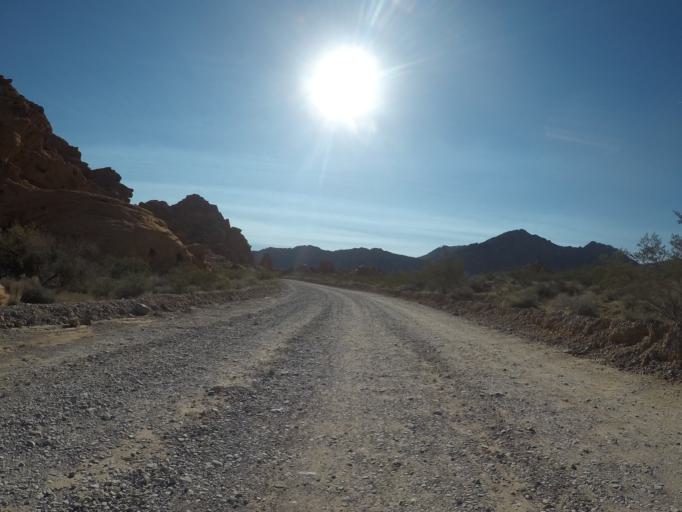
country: US
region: Nevada
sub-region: Clark County
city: Moapa Valley
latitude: 36.4161
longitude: -114.5594
